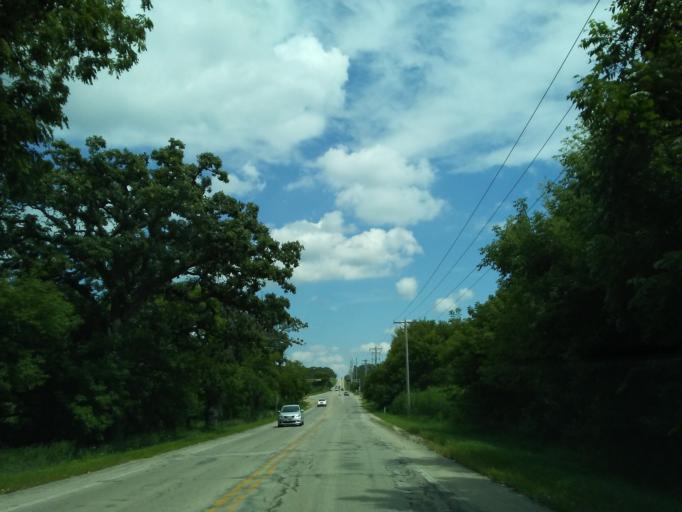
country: US
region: Wisconsin
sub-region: Dane County
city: Verona
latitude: 43.0161
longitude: -89.5364
